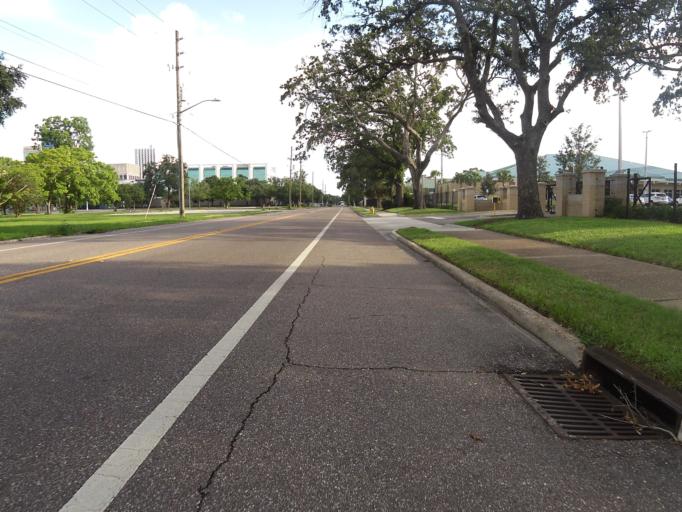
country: US
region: Florida
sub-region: Duval County
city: Jacksonville
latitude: 30.3376
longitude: -81.6638
